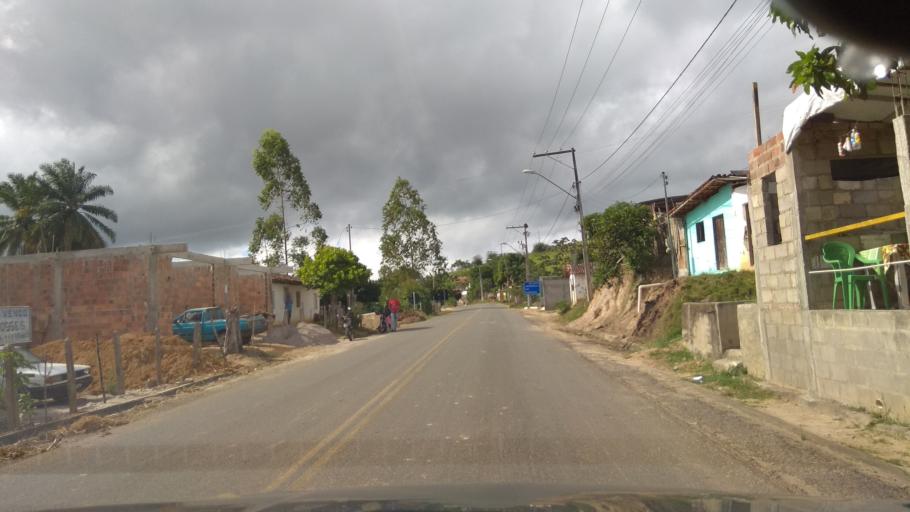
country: BR
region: Bahia
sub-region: Ubaira
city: Ubaira
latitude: -13.2542
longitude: -39.5875
